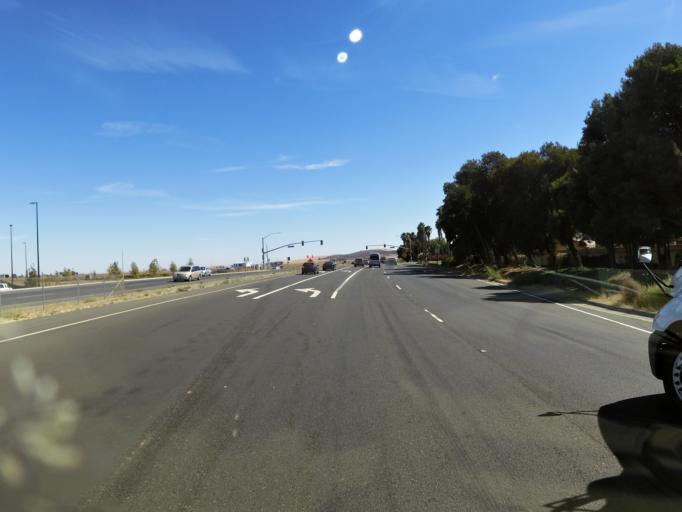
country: US
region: California
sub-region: Solano County
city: Suisun
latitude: 38.2412
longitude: -121.9912
